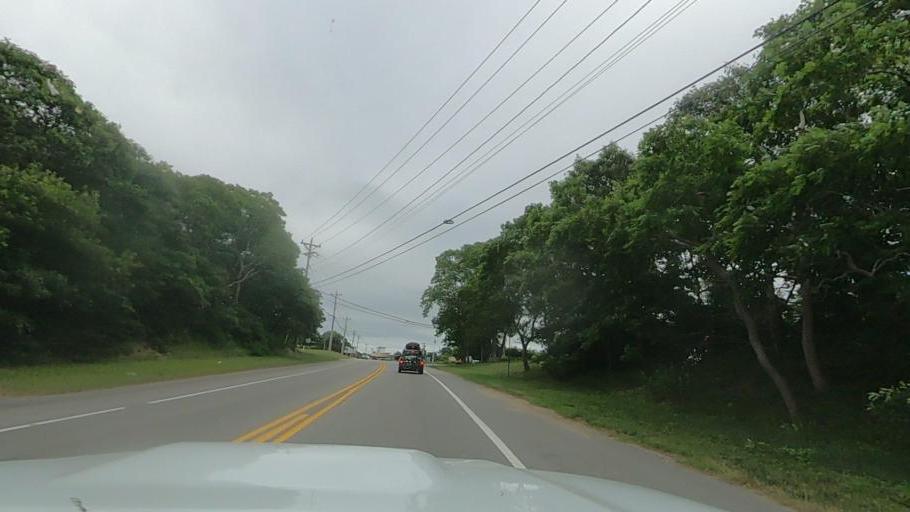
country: US
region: Massachusetts
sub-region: Barnstable County
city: Truro
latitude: 42.0249
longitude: -70.0760
